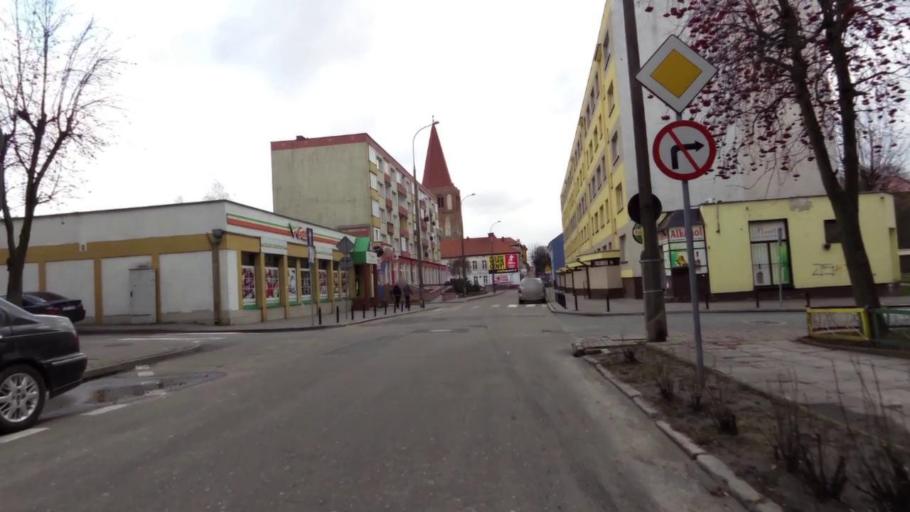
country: PL
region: West Pomeranian Voivodeship
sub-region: Powiat mysliborski
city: Mysliborz
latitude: 52.9263
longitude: 14.8658
